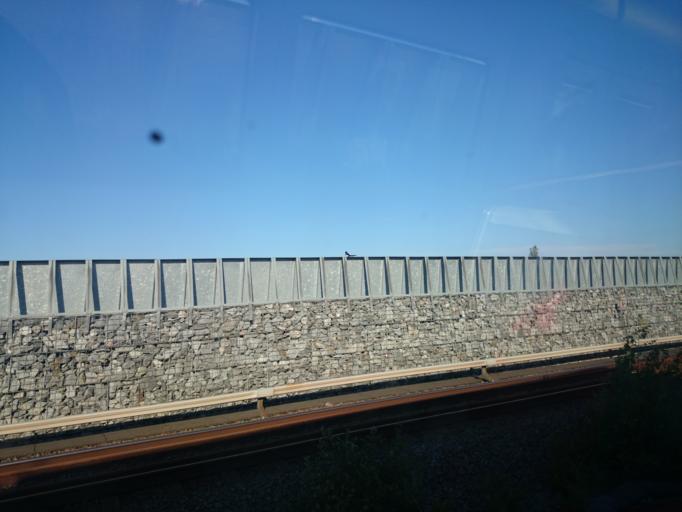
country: DK
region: Capital Region
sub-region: Dragor Kommune
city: Dragor
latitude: 55.6334
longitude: 12.6484
